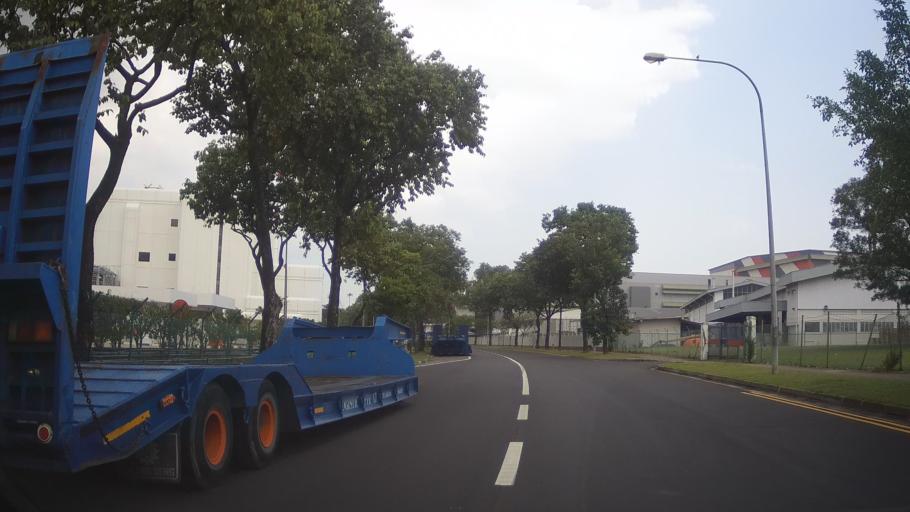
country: MY
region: Johor
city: Johor Bahru
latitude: 1.3071
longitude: 103.6609
